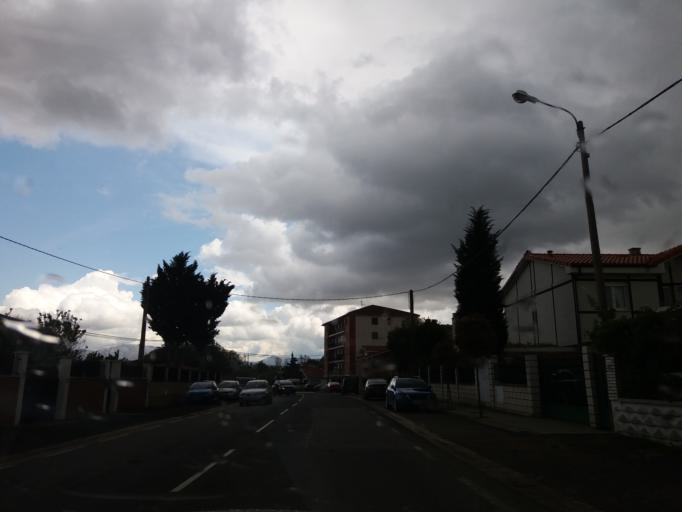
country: ES
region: La Rioja
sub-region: Provincia de La Rioja
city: Anguciana
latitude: 42.5754
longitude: -2.9100
